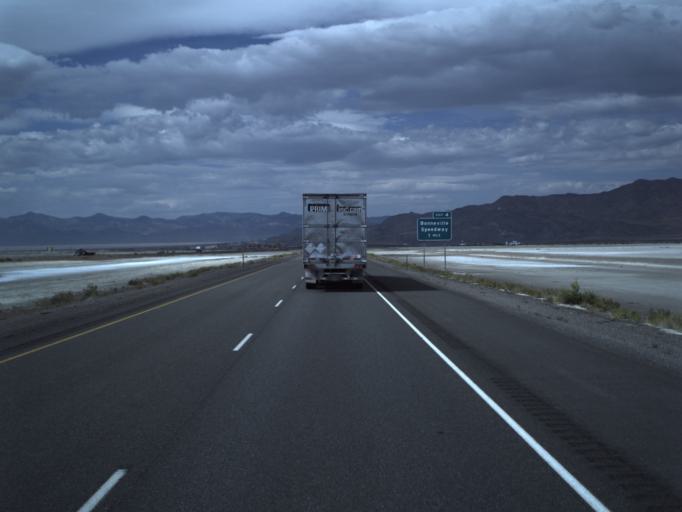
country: US
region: Utah
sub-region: Tooele County
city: Wendover
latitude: 40.7412
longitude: -113.9418
